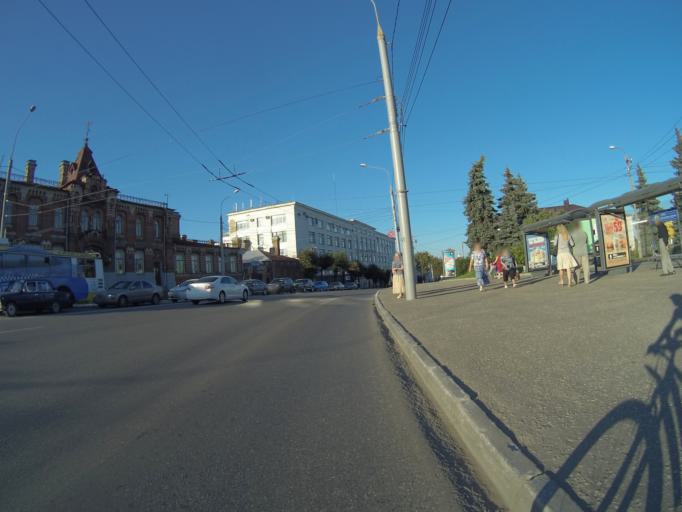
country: RU
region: Vladimir
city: Vladimir
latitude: 56.1252
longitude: 40.3871
